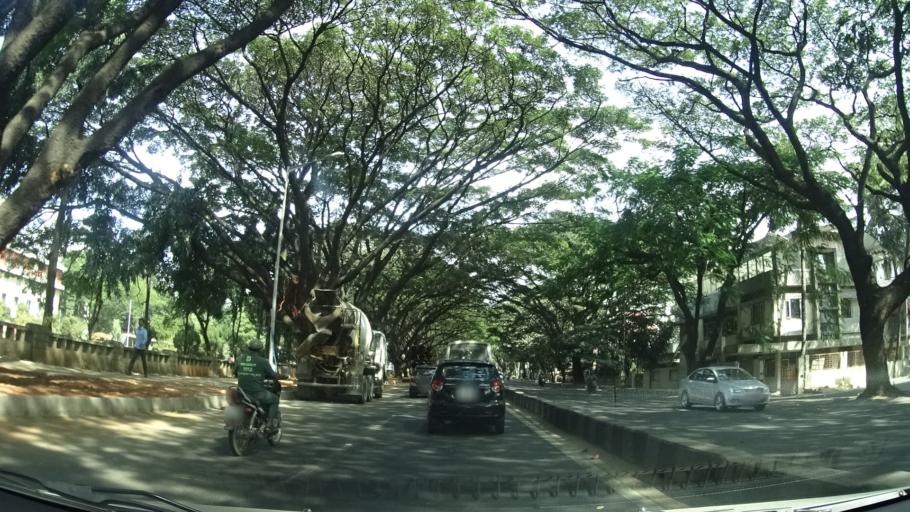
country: IN
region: Karnataka
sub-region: Bangalore Urban
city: Bangalore
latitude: 13.0149
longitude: 77.5734
